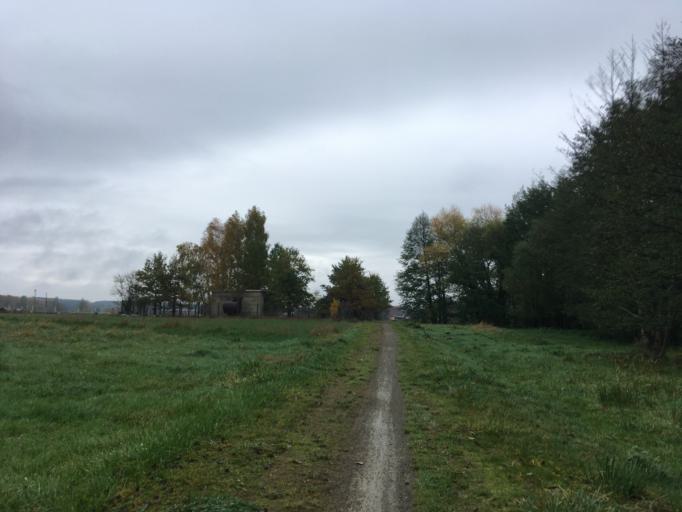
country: DE
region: Brandenburg
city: Friedland
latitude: 52.0342
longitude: 14.1771
